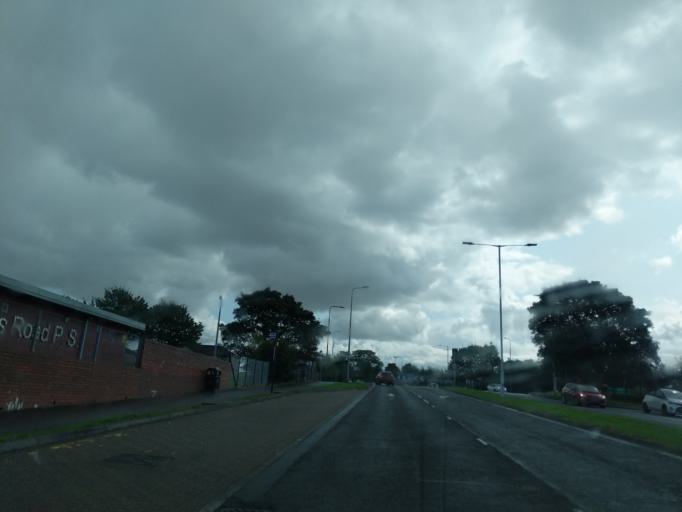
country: GB
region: Scotland
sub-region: Fife
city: Rosyth
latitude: 56.0372
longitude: -3.4279
